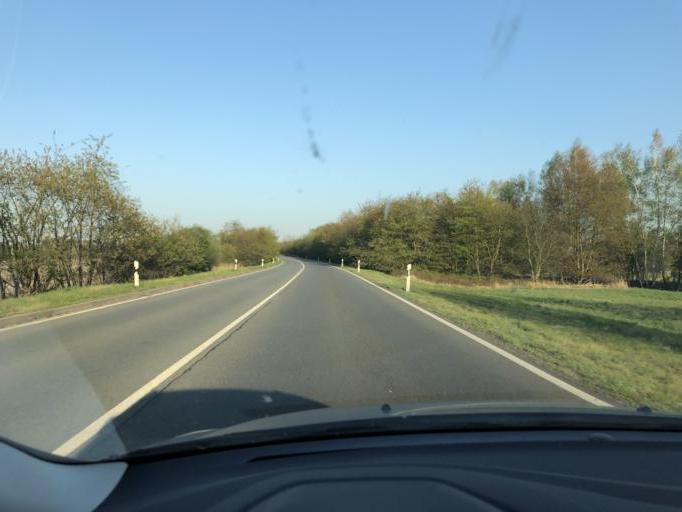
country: DE
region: Brandenburg
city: Ruhland
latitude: 51.4648
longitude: 13.8715
